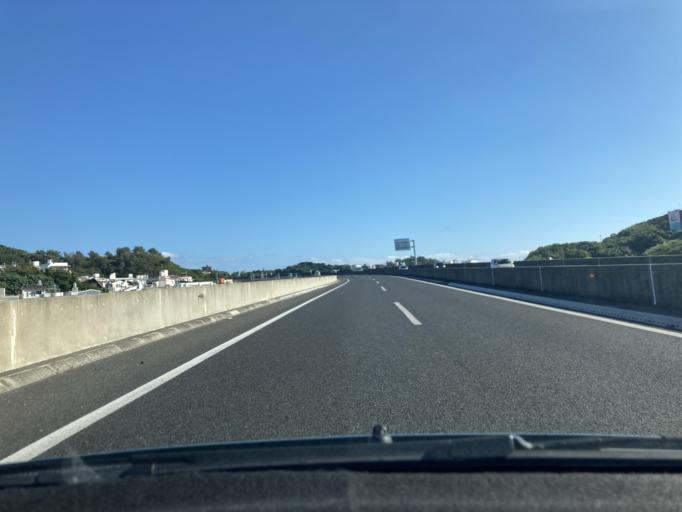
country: JP
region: Okinawa
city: Tomigusuku
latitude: 26.1739
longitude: 127.6756
